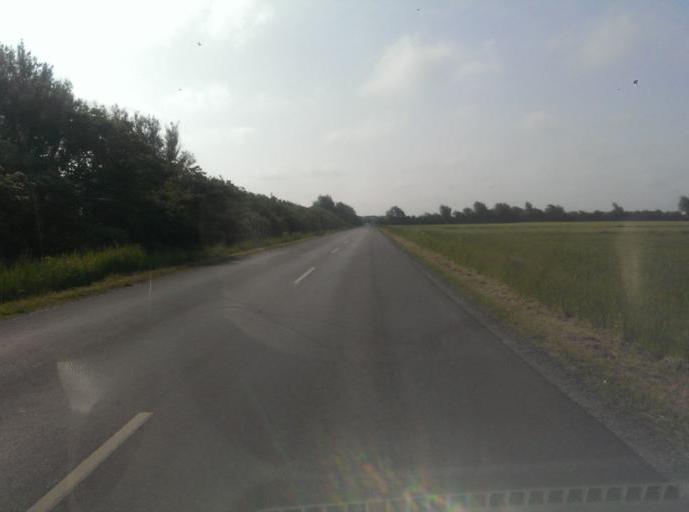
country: DK
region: South Denmark
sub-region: Esbjerg Kommune
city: Tjaereborg
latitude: 55.4377
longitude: 8.6297
